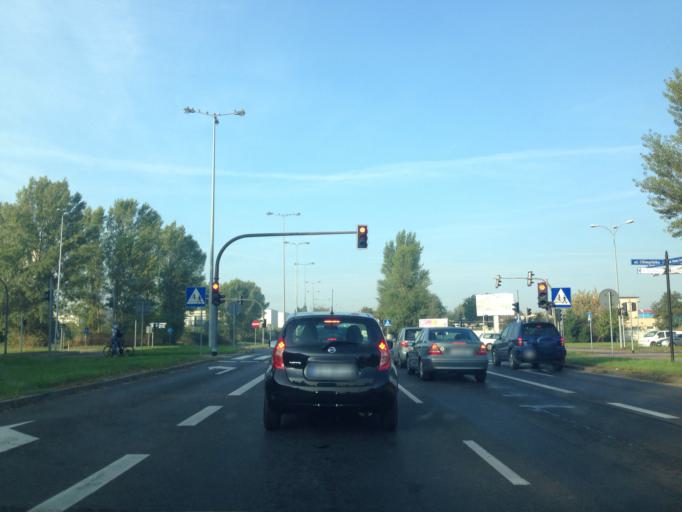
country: PL
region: Kujawsko-Pomorskie
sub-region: Powiat torunski
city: Lubicz Dolny
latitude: 53.0313
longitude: 18.7015
